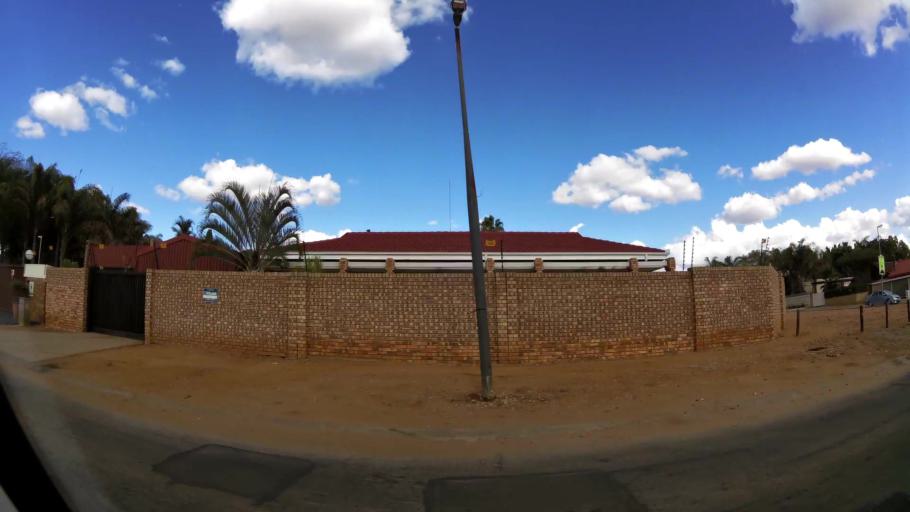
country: ZA
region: Limpopo
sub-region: Capricorn District Municipality
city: Polokwane
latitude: -23.8959
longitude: 29.4749
